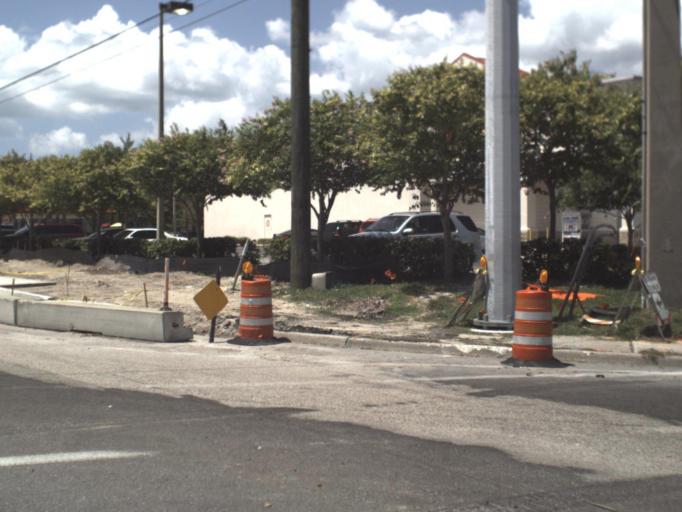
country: US
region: Florida
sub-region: Pinellas County
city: South Highpoint
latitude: 27.8944
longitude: -82.7459
